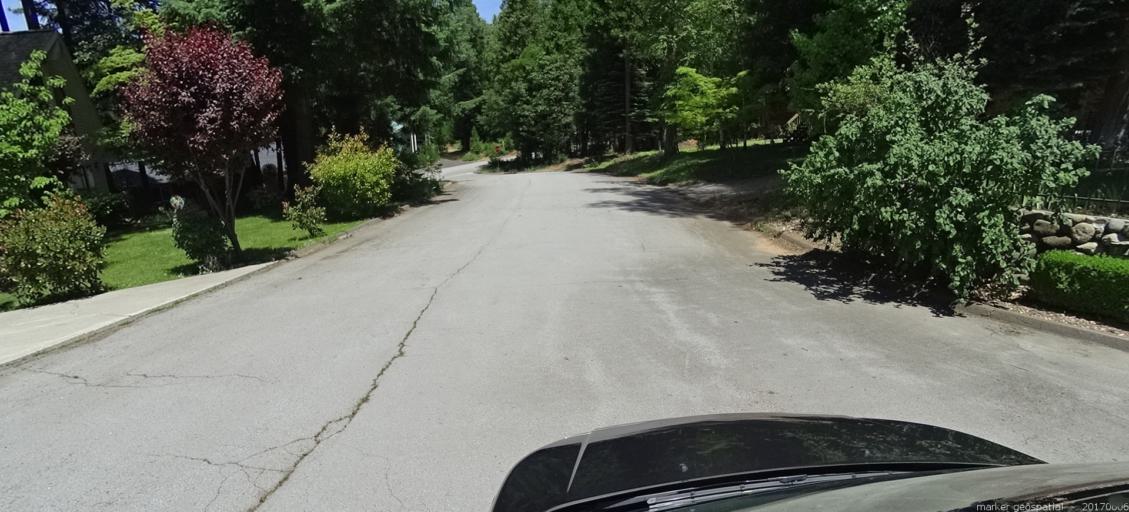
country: US
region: California
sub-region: Siskiyou County
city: Dunsmuir
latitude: 41.2298
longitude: -122.2733
